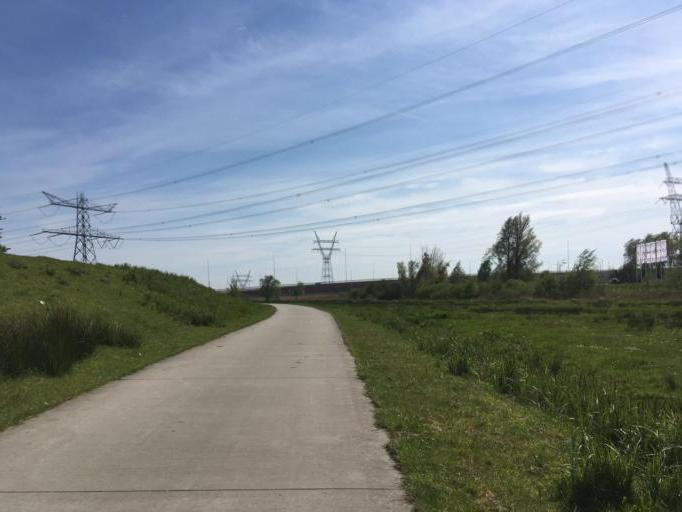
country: NL
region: North Holland
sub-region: Gemeente Amsterdam
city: Driemond
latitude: 52.3351
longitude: 5.0270
